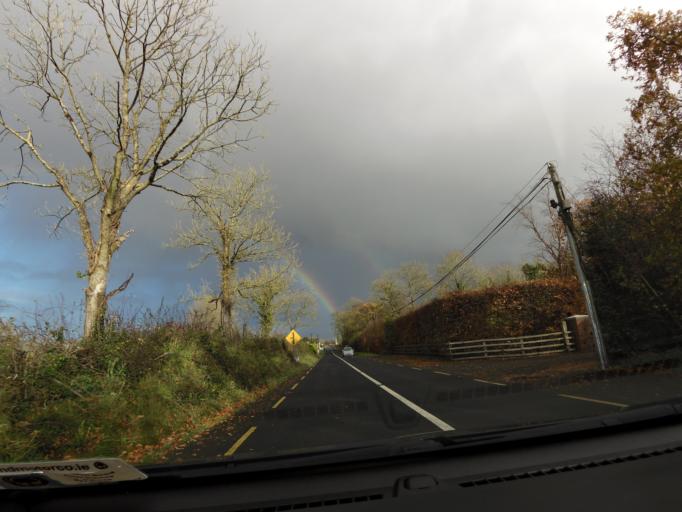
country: IE
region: Munster
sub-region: North Tipperary
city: Newport
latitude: 52.7085
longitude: -8.4302
